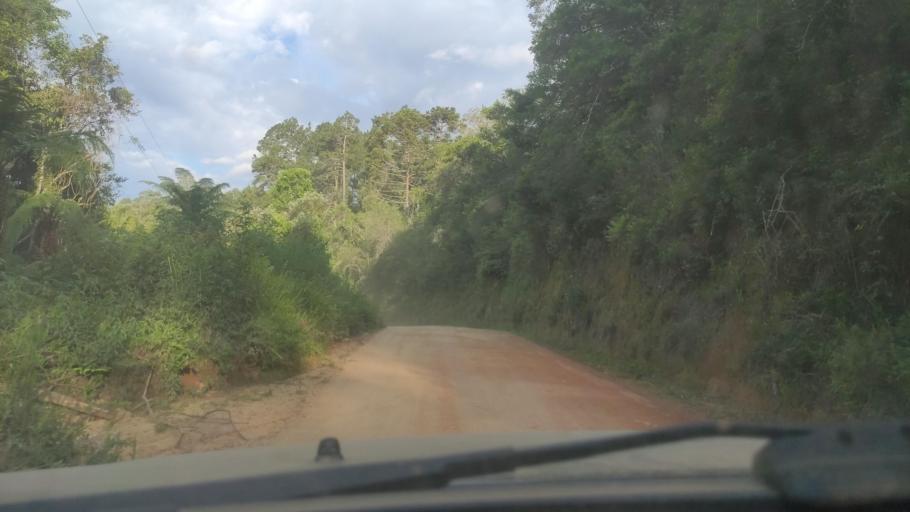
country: BR
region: Minas Gerais
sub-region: Cambui
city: Cambui
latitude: -22.7511
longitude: -45.9316
